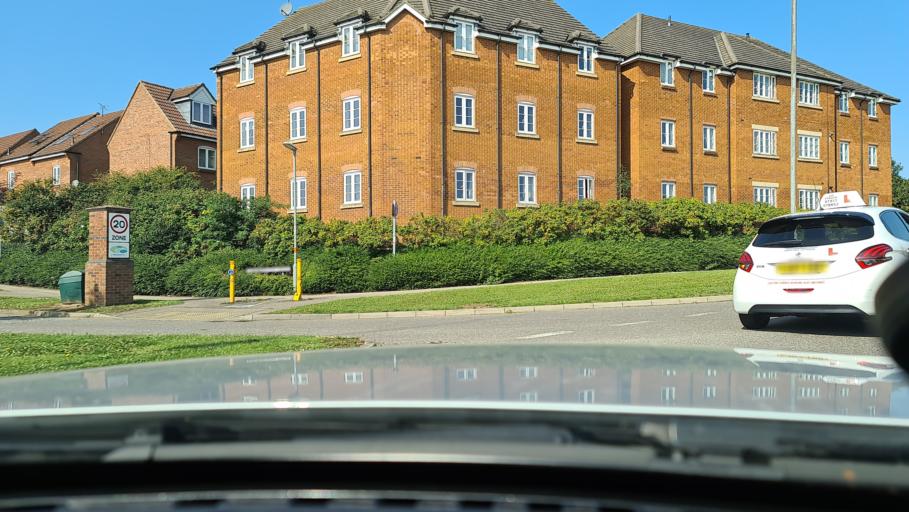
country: GB
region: England
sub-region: Northamptonshire
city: Daventry
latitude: 52.2817
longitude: -1.1684
